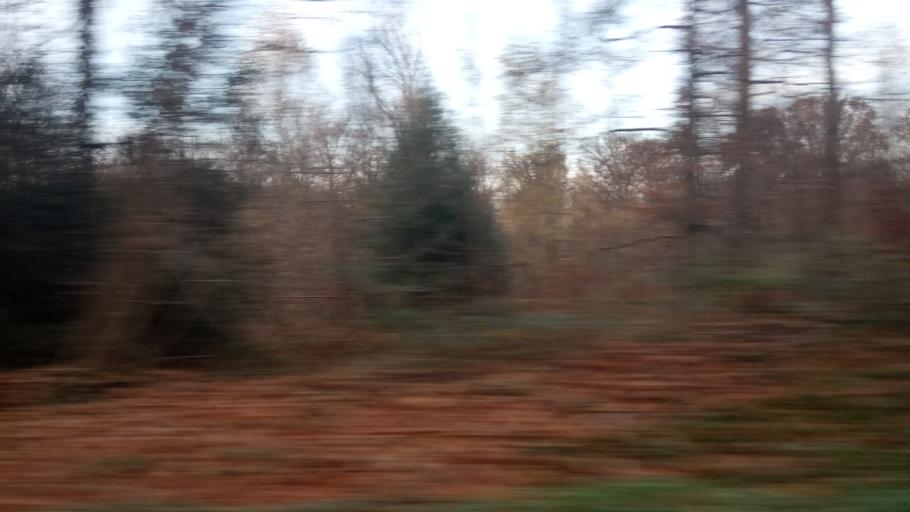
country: DE
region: North Rhine-Westphalia
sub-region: Regierungsbezirk Dusseldorf
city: Velbert
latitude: 51.3815
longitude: 7.0557
